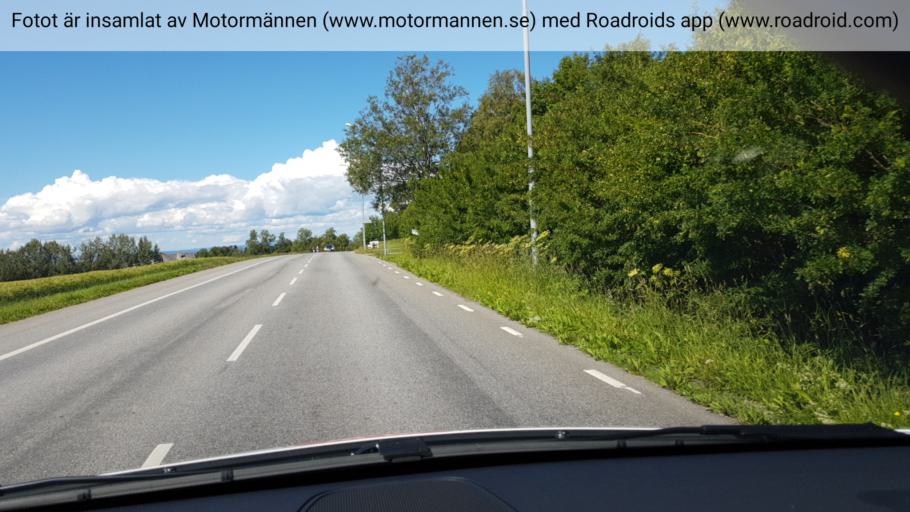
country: SE
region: Jaemtland
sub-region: Krokoms Kommun
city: Krokom
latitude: 63.1971
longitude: 14.4772
